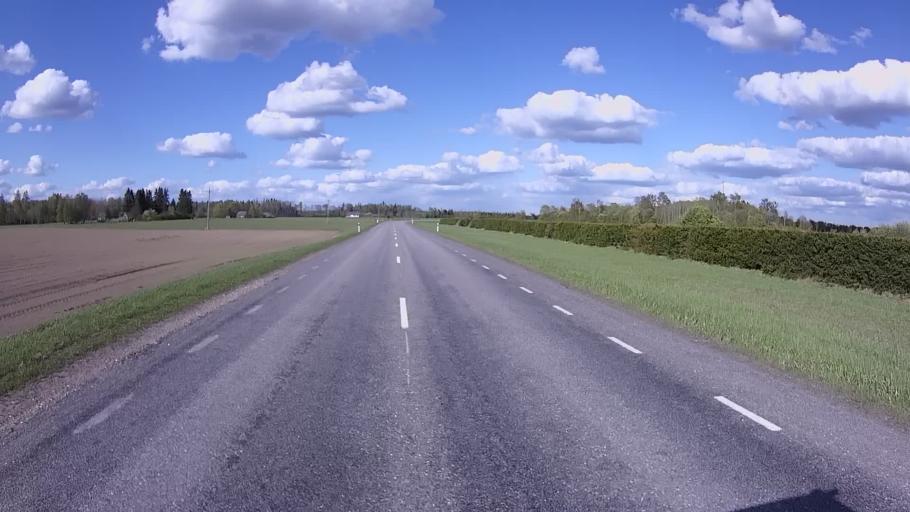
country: EE
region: Jogevamaa
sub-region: Poltsamaa linn
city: Poltsamaa
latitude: 58.6935
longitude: 26.1342
